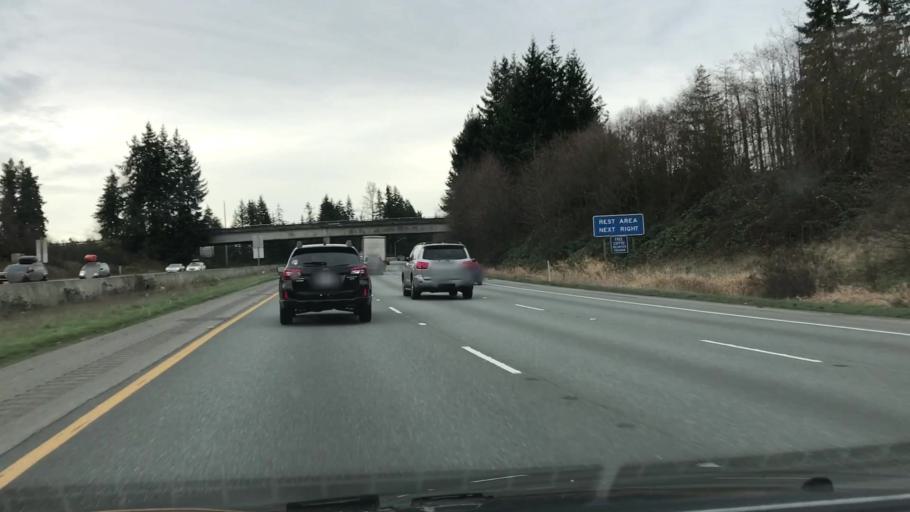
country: US
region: Washington
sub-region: Snohomish County
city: Smokey Point
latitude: 48.1779
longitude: -122.1942
